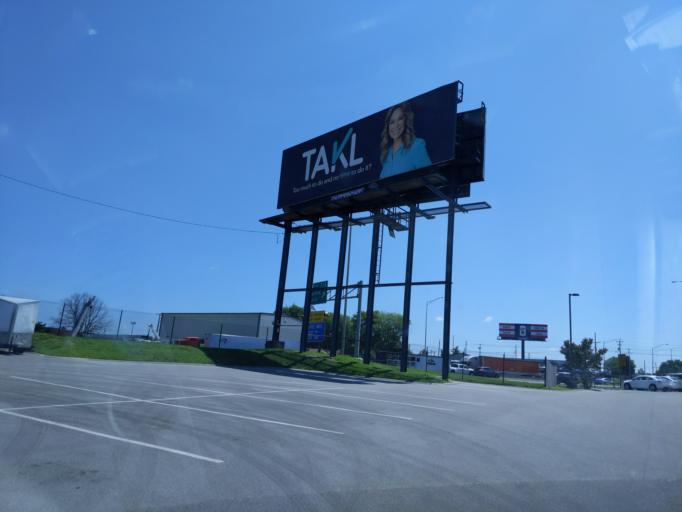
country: US
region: Tennessee
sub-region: Davidson County
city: Nashville
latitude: 36.1484
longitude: -86.7468
